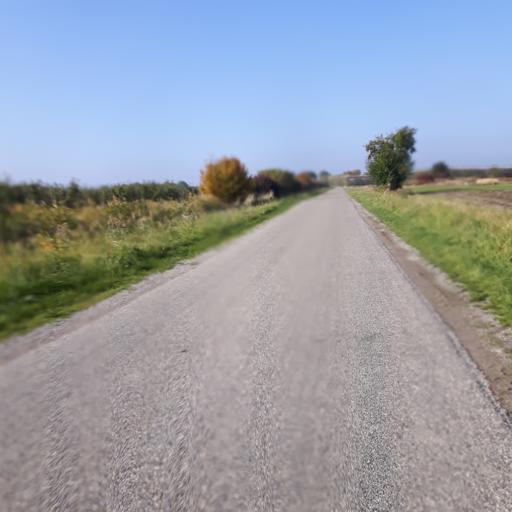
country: NL
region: Zeeland
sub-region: Gemeente Reimerswaal
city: Yerseke
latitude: 51.4851
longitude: 3.9814
